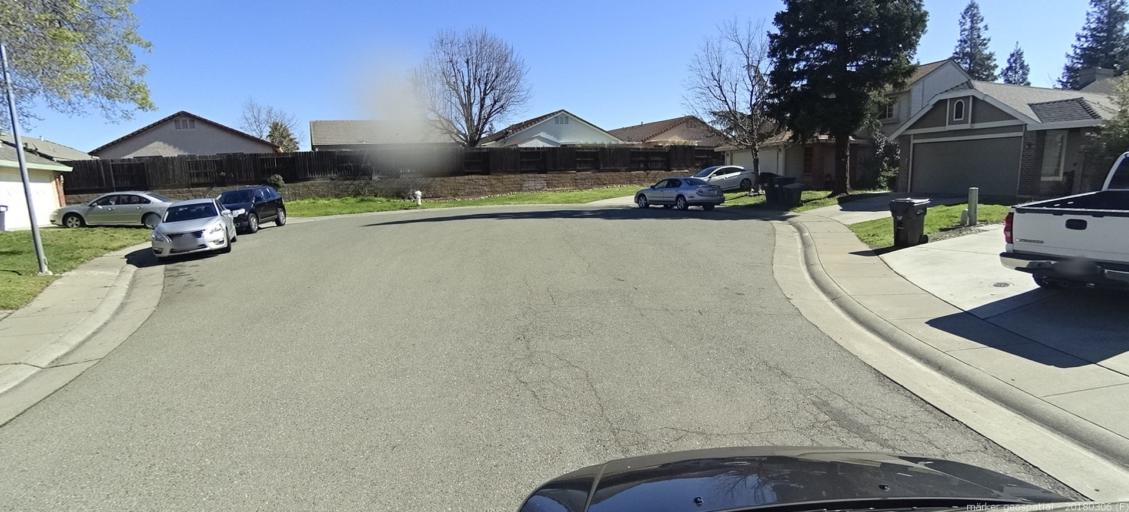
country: US
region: California
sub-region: Sacramento County
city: Vineyard
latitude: 38.4631
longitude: -121.3568
